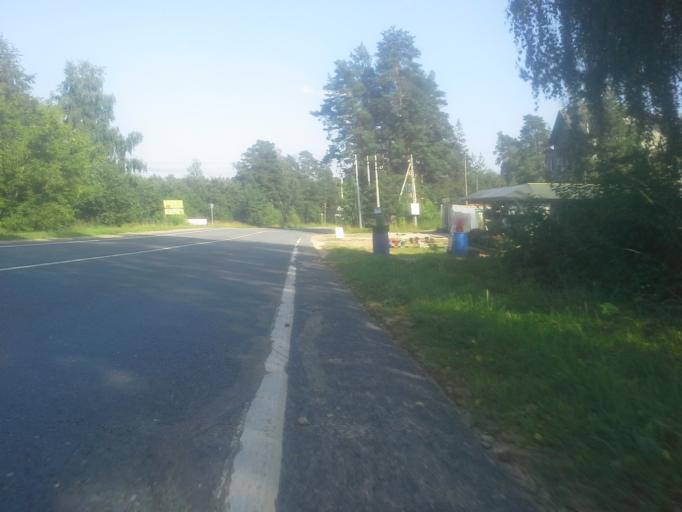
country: RU
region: Moskovskaya
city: Karinskoye
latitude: 55.7049
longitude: 36.7685
